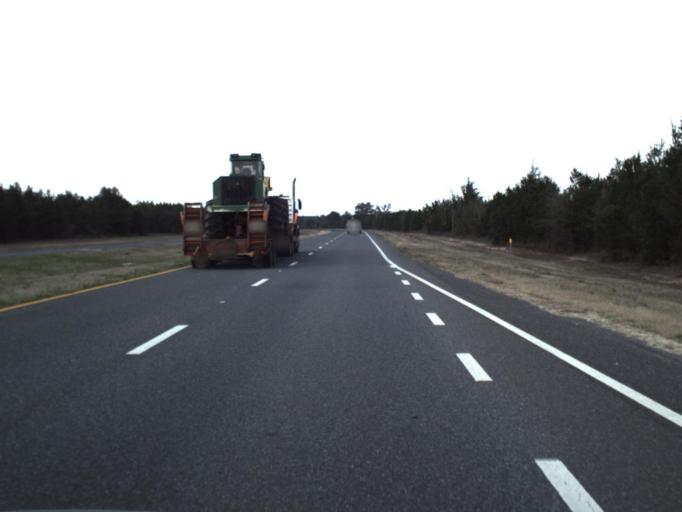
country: US
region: Florida
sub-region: Bay County
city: Youngstown
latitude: 30.5384
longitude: -85.3929
